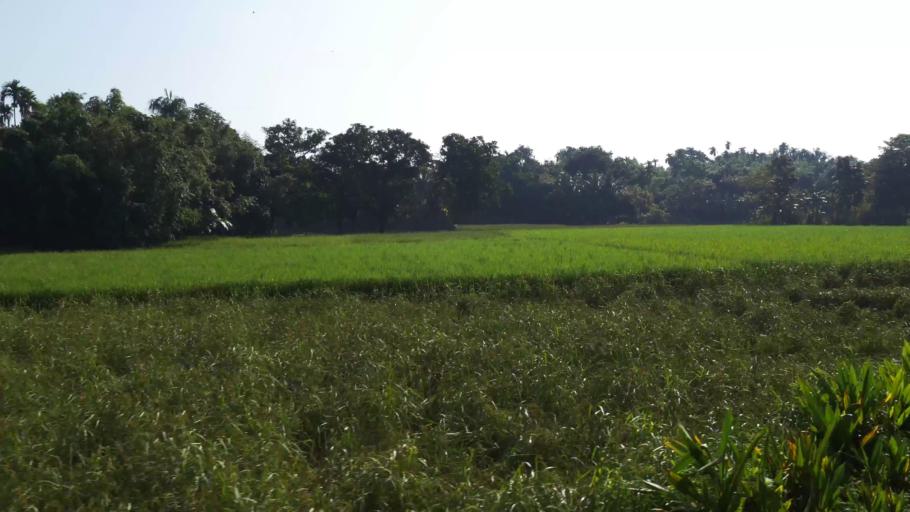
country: BD
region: Dhaka
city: Muktagacha
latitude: 24.8095
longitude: 90.2987
